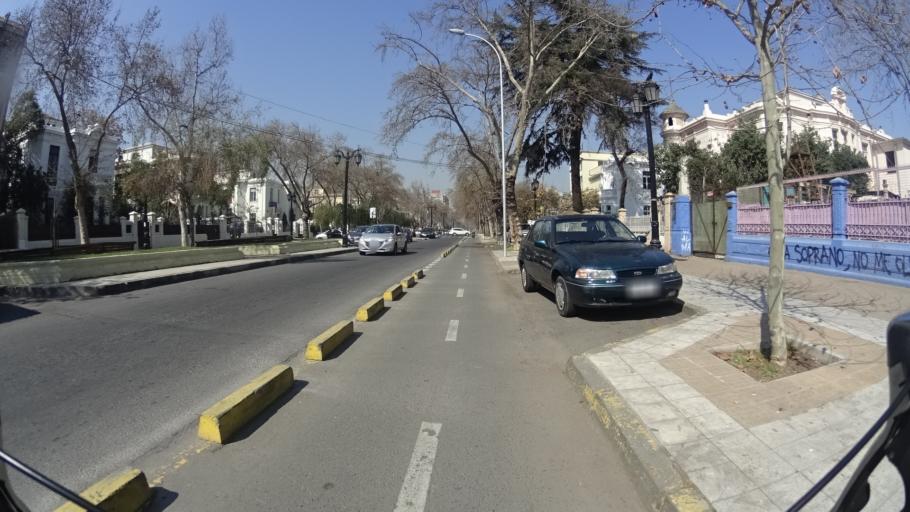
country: CL
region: Santiago Metropolitan
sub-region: Provincia de Santiago
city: Santiago
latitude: -33.4524
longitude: -70.6675
